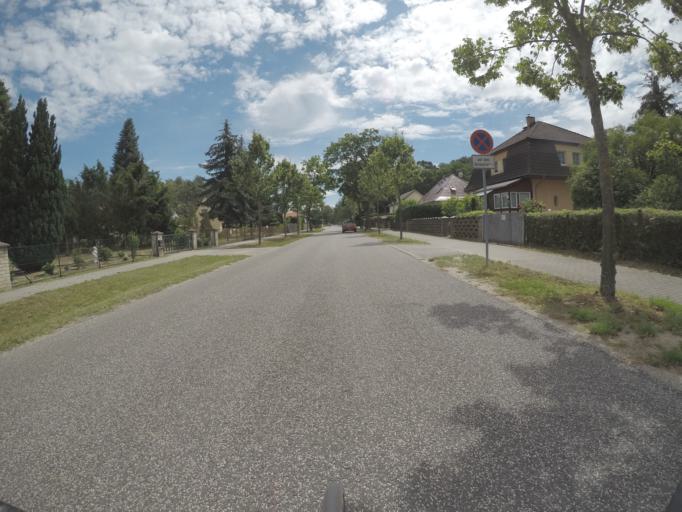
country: DE
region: Brandenburg
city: Storkow
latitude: 52.2476
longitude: 13.9480
